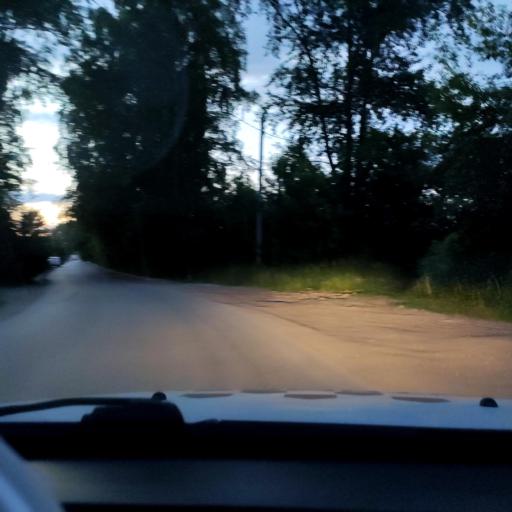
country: RU
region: Perm
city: Overyata
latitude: 58.0132
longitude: 55.9428
